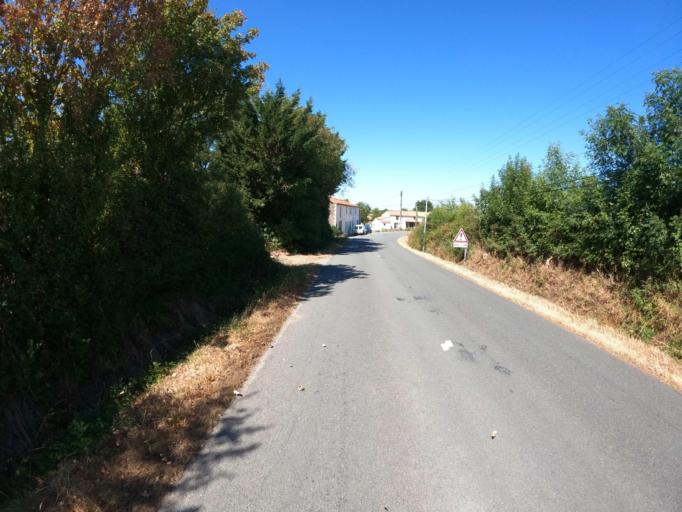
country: FR
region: Pays de la Loire
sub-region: Departement de la Vendee
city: Saint-Aubin-des-Ormeaux
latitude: 46.9971
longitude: -1.0312
